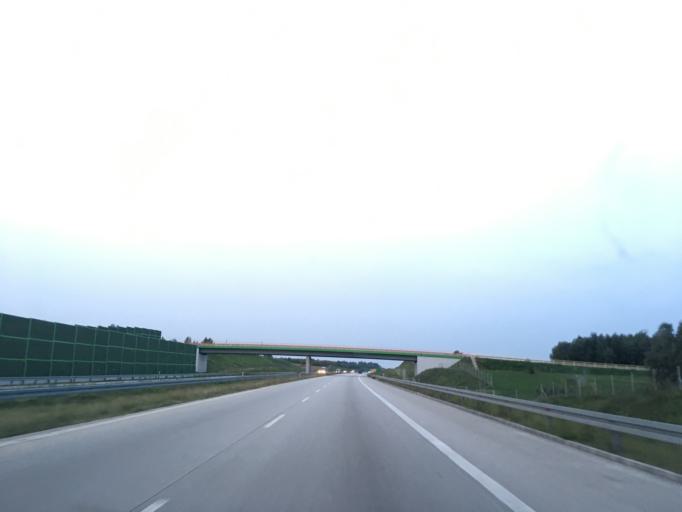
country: PL
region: Lodz Voivodeship
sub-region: Powiat zgierski
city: Strykow
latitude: 51.8230
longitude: 19.6482
